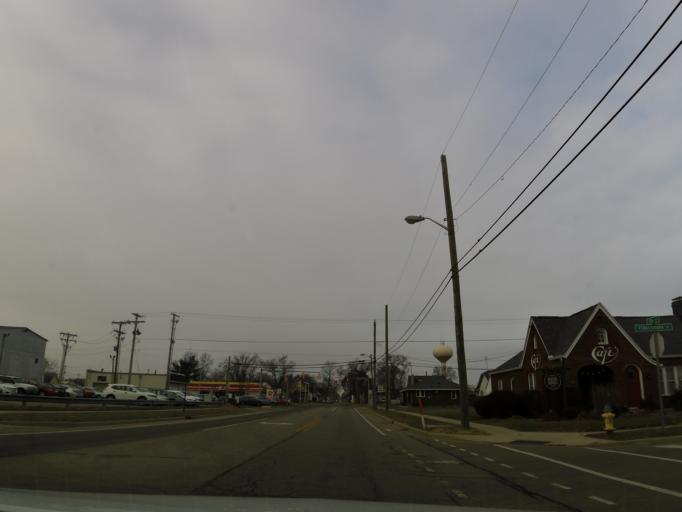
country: US
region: Indiana
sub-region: Bartholomew County
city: Columbus
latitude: 39.2159
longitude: -85.9028
